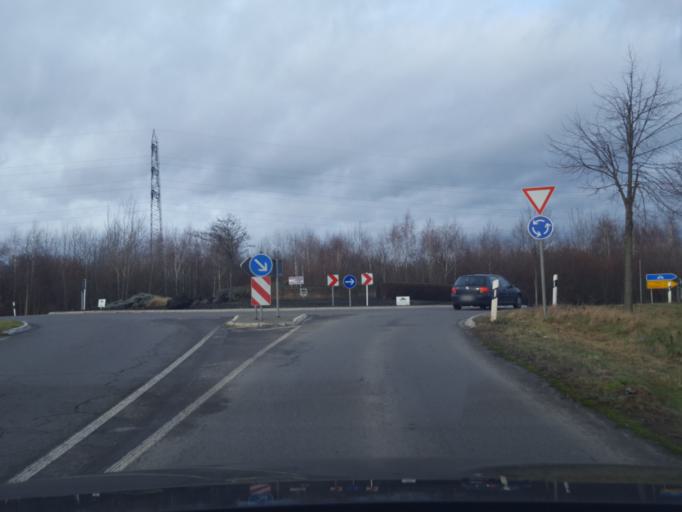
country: DE
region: North Rhine-Westphalia
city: Niederkassel
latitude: 50.8253
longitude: 7.0445
